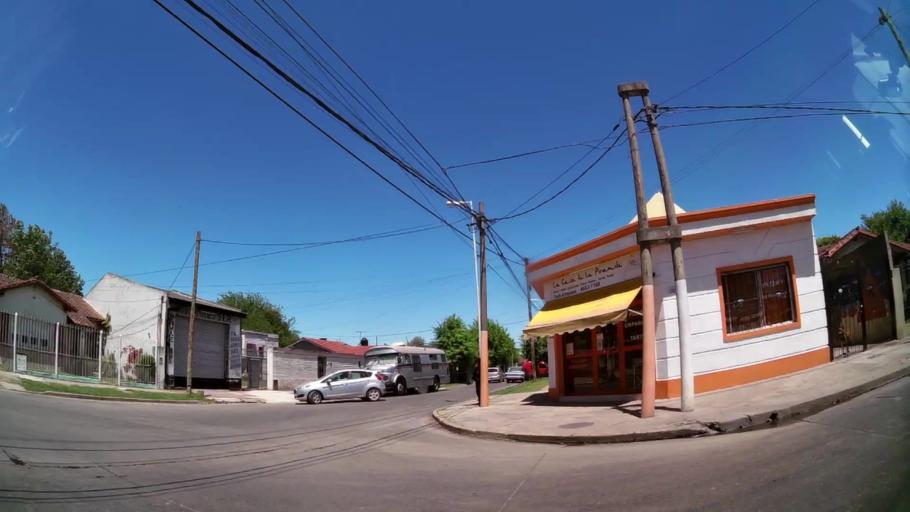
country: AR
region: Buenos Aires
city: Hurlingham
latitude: -34.5139
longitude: -58.7081
